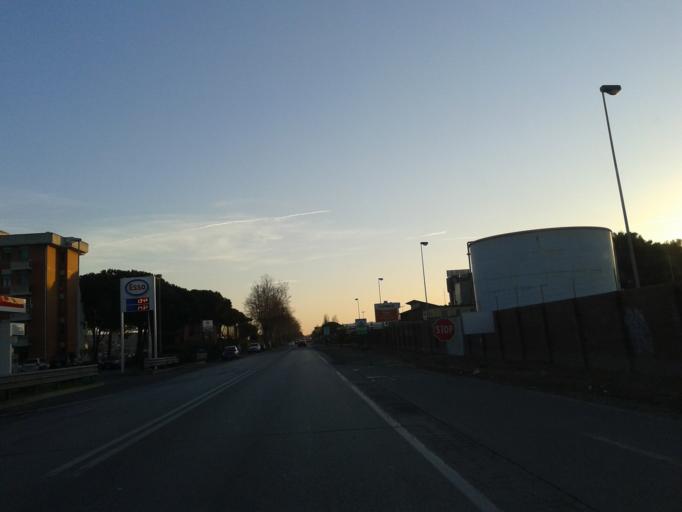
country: IT
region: Tuscany
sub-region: Provincia di Livorno
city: Livorno
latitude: 43.5918
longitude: 10.3484
